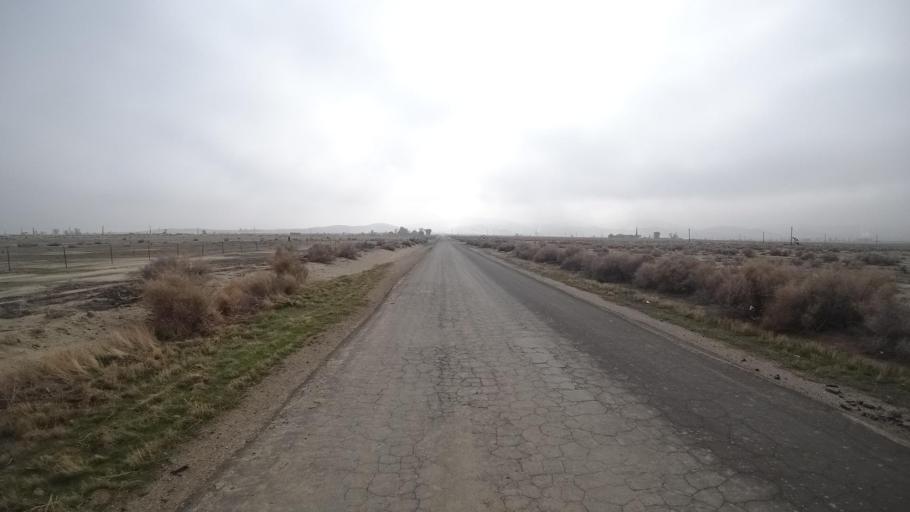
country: US
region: California
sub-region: Kern County
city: Maricopa
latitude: 35.0523
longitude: -119.3671
